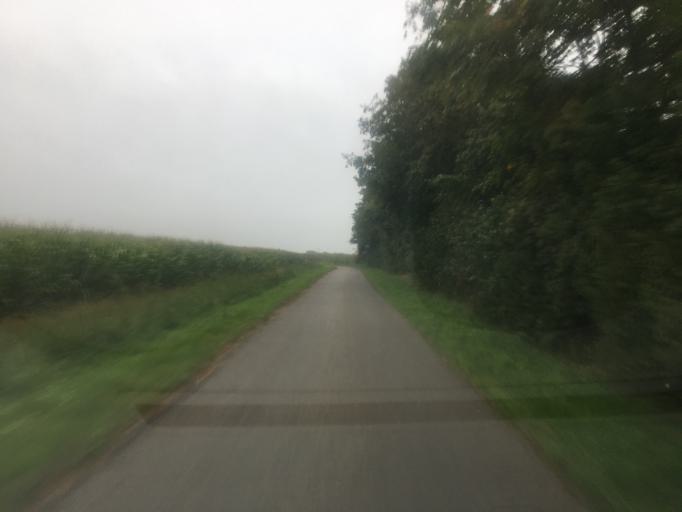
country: DK
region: South Denmark
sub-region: Tonder Kommune
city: Logumkloster
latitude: 55.0425
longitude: 8.9123
